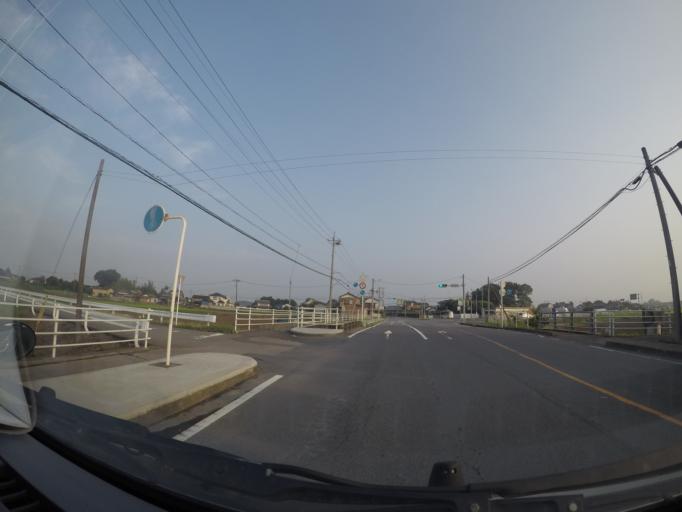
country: JP
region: Tochigi
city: Fujioka
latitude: 36.2787
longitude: 139.7091
